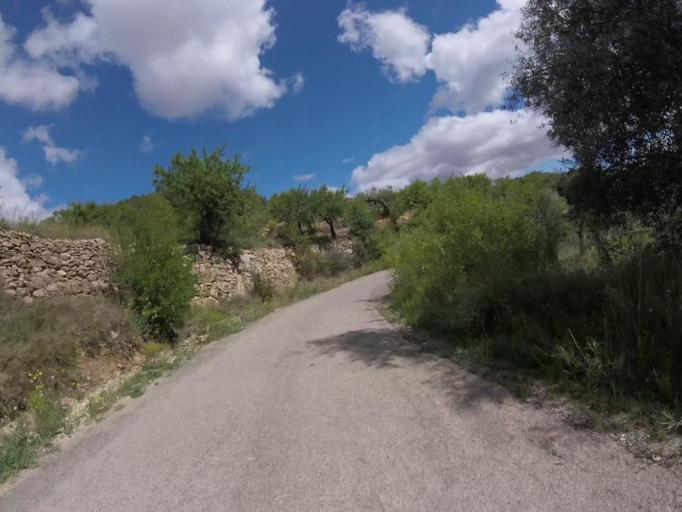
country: ES
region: Valencia
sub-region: Provincia de Castello
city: Sierra-Engarceran
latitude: 40.2721
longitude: -0.0917
